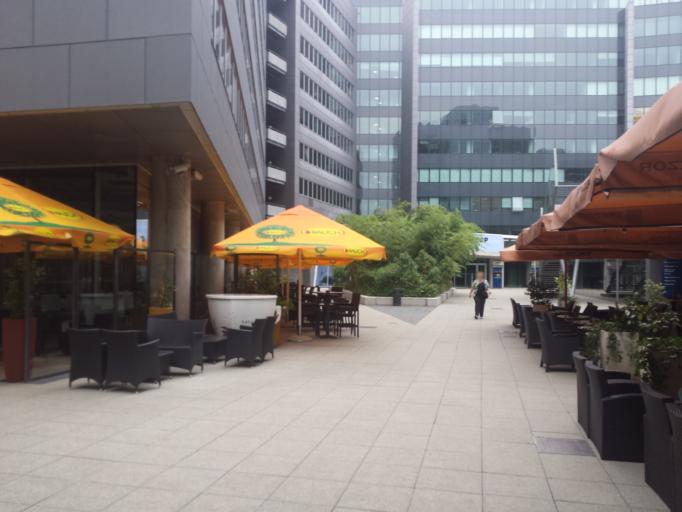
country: HR
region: Grad Zagreb
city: Novi Zagreb
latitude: 45.7931
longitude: 15.9697
